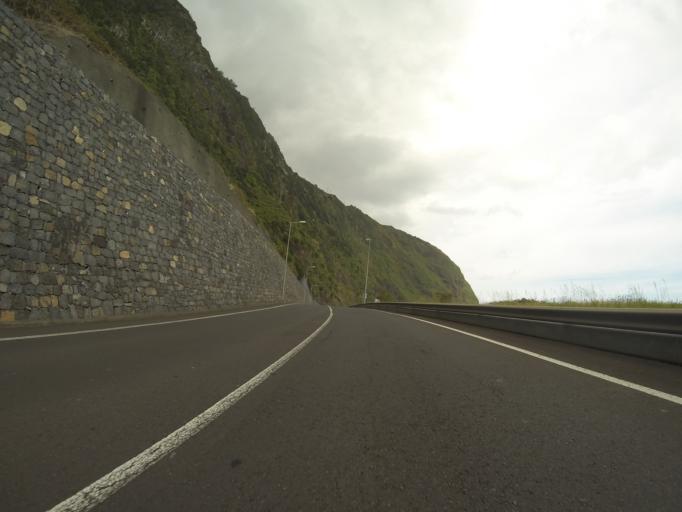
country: PT
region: Madeira
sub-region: Porto Moniz
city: Porto Moniz
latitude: 32.8470
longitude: -17.1482
